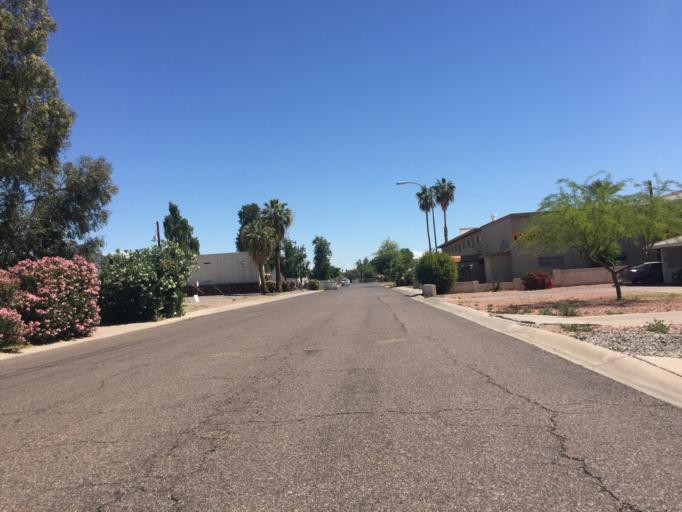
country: US
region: Arizona
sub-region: Maricopa County
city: Phoenix
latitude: 33.5292
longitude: -112.0638
